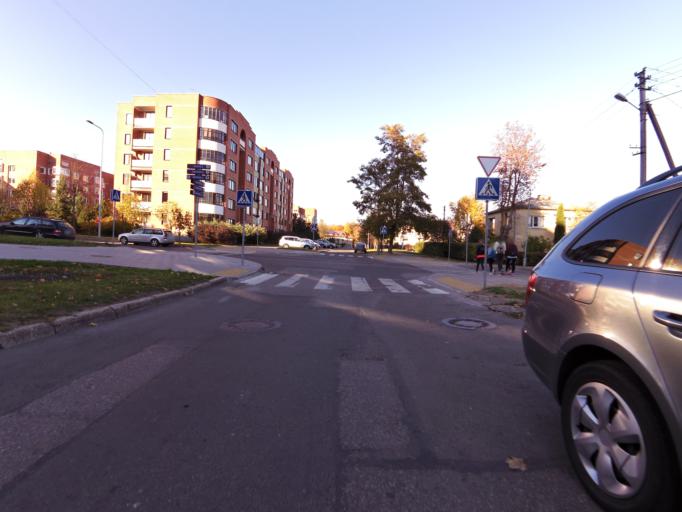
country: LT
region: Vilnius County
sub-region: Vilnius
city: Fabijoniskes
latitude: 54.7437
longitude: 25.2726
